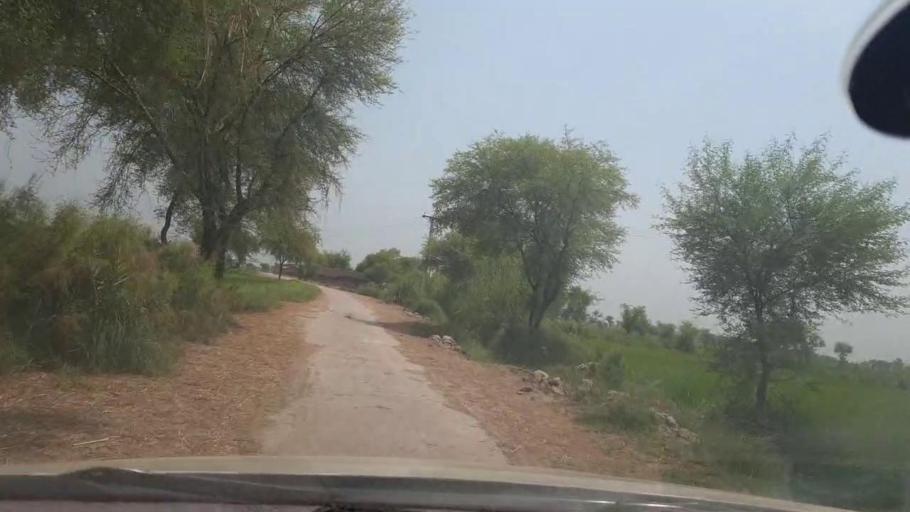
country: PK
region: Sindh
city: Jacobabad
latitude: 28.1761
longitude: 68.3847
